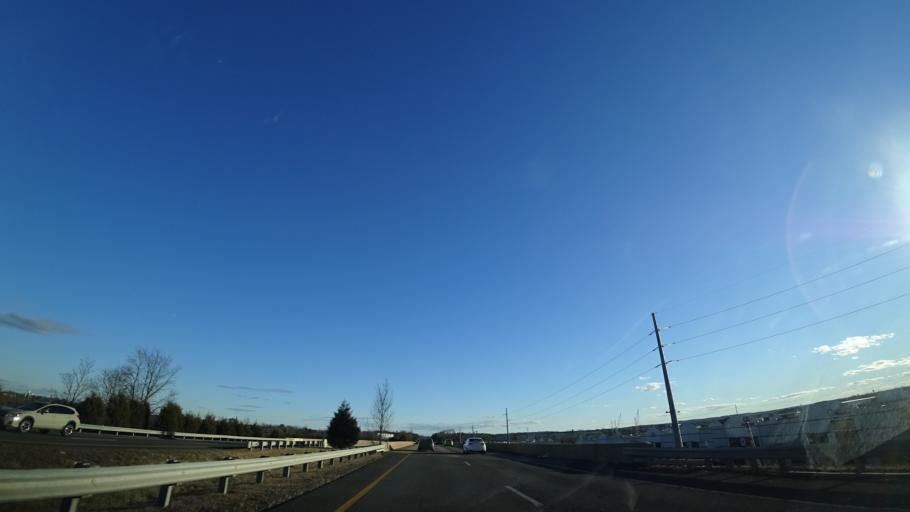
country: US
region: Virginia
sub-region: Prince William County
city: Bull Run
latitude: 38.7860
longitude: -77.5495
